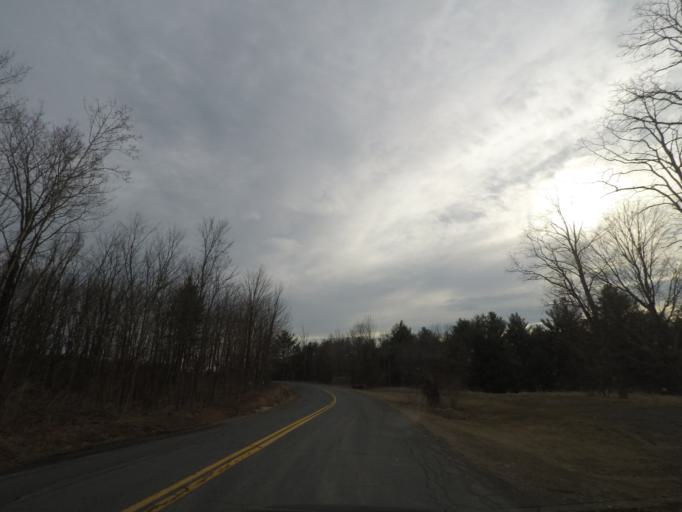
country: US
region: New York
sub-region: Rensselaer County
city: Hoosick Falls
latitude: 42.8639
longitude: -73.4502
